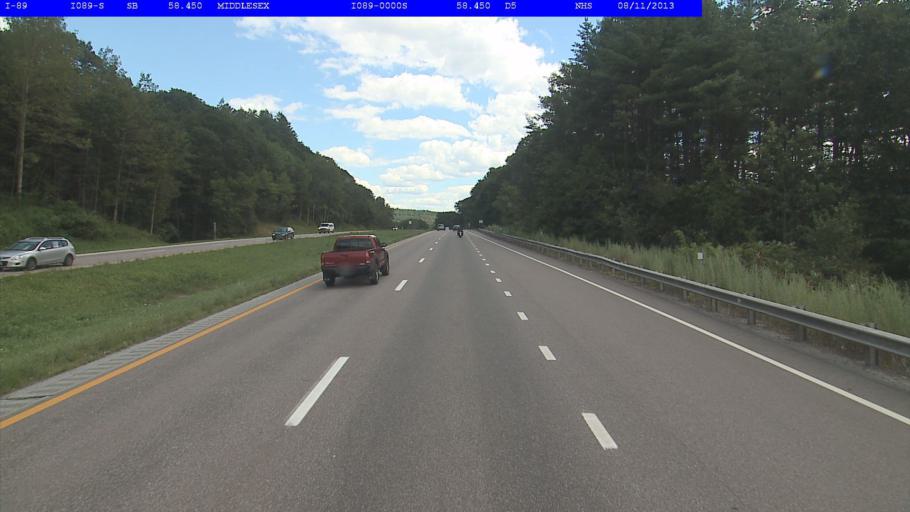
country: US
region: Vermont
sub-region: Washington County
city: Waterbury
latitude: 44.2957
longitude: -72.6813
